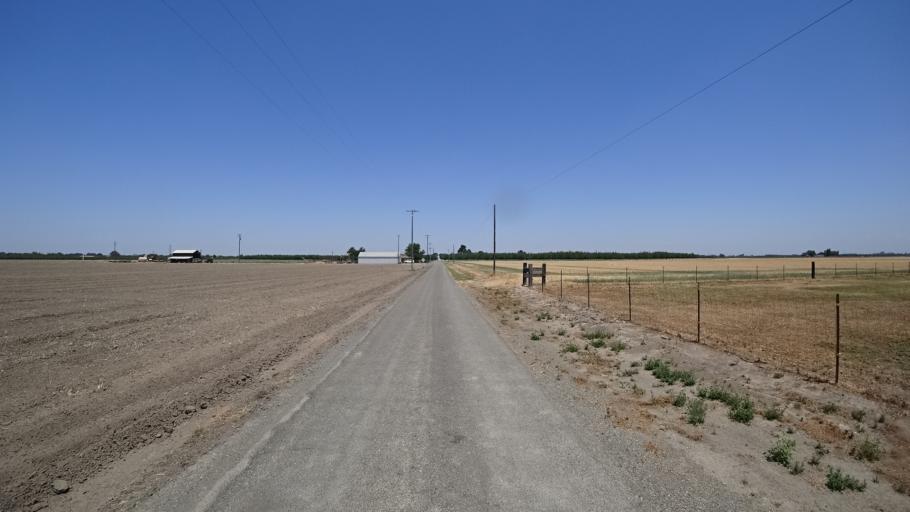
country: US
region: California
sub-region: Fresno County
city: Laton
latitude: 36.3870
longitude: -119.7367
